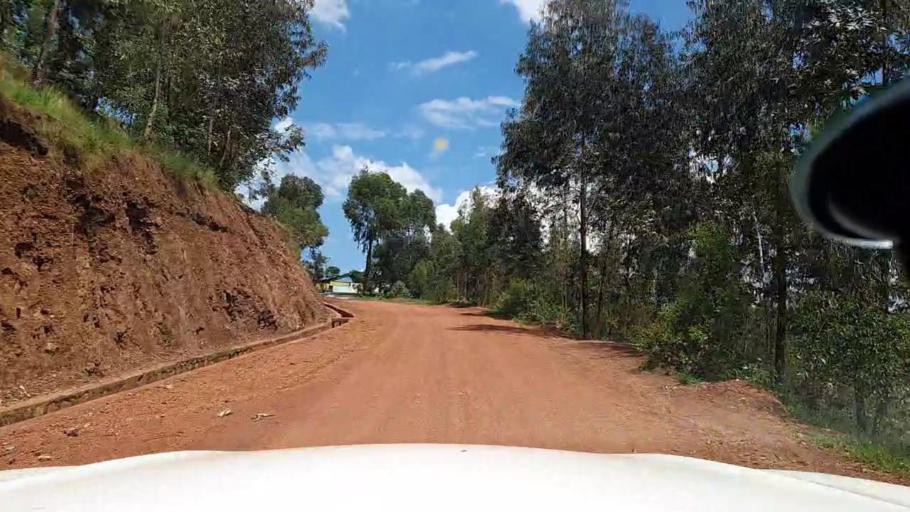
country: RW
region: Northern Province
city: Byumba
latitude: -1.7371
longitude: 29.8576
